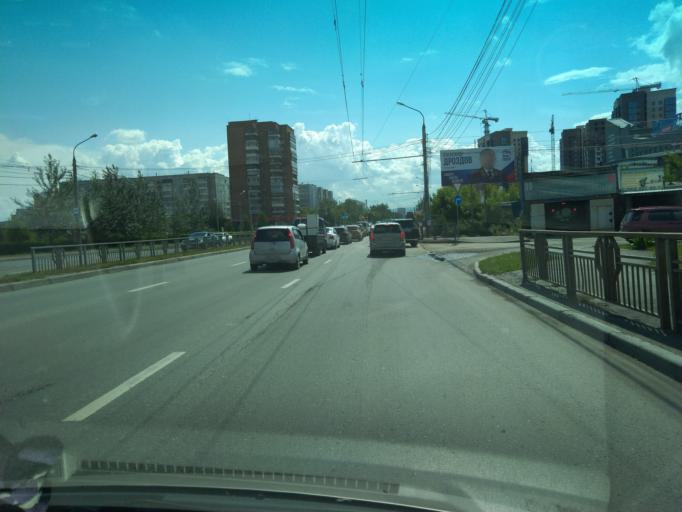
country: RU
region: Krasnoyarskiy
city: Solnechnyy
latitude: 56.0559
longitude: 92.9412
